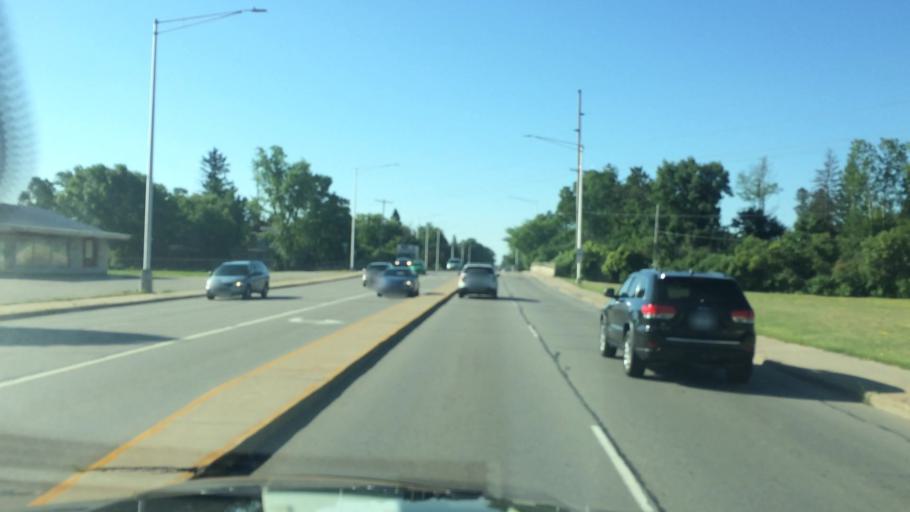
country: US
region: Wisconsin
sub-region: Marathon County
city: Wausau
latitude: 44.9508
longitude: -89.6225
